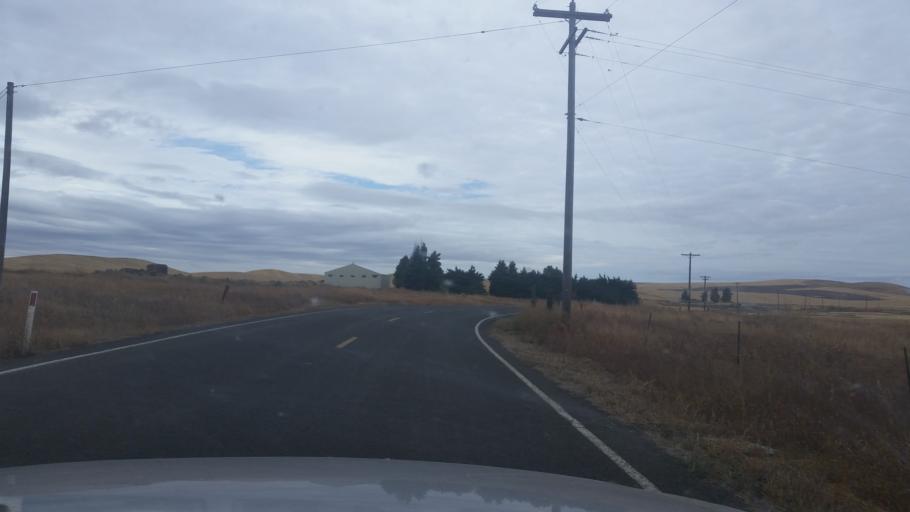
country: US
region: Washington
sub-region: Spokane County
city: Medical Lake
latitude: 47.5176
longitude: -117.8946
